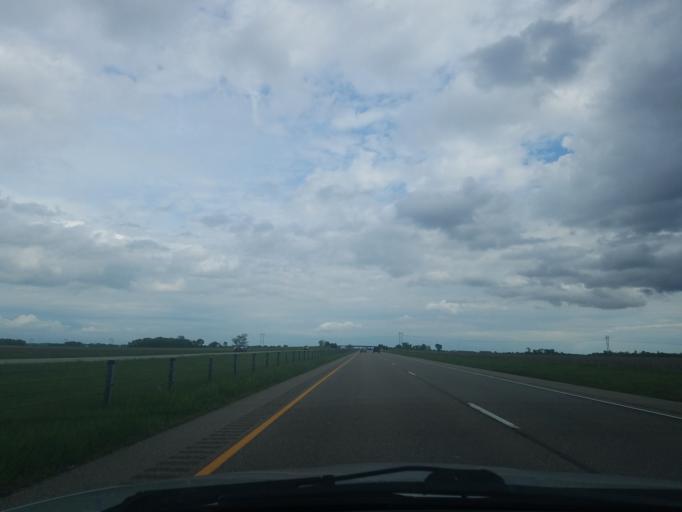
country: US
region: Minnesota
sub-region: Clay County
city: Glyndon
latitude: 46.8159
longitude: -96.5988
